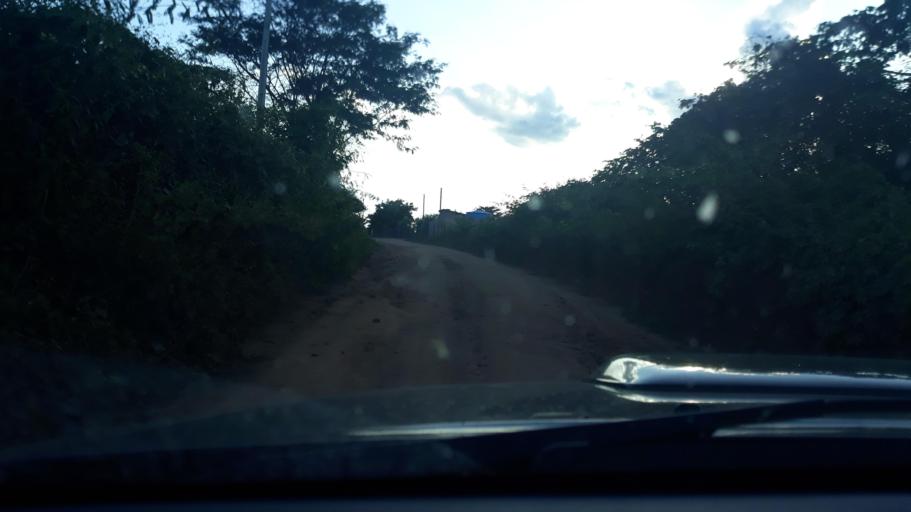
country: BR
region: Bahia
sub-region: Riacho De Santana
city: Riacho de Santana
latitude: -13.8076
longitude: -42.7163
